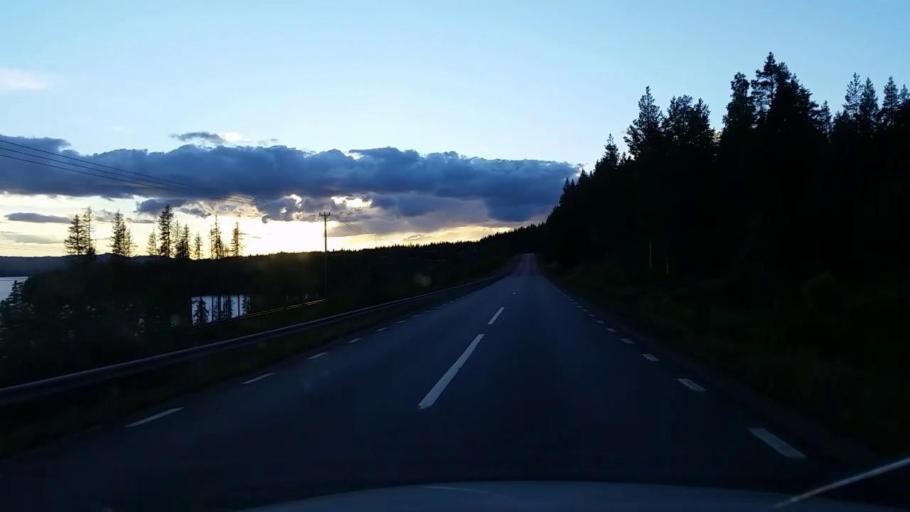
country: SE
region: Gaevleborg
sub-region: Ljusdals Kommun
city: Farila
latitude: 62.1049
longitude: 15.7745
